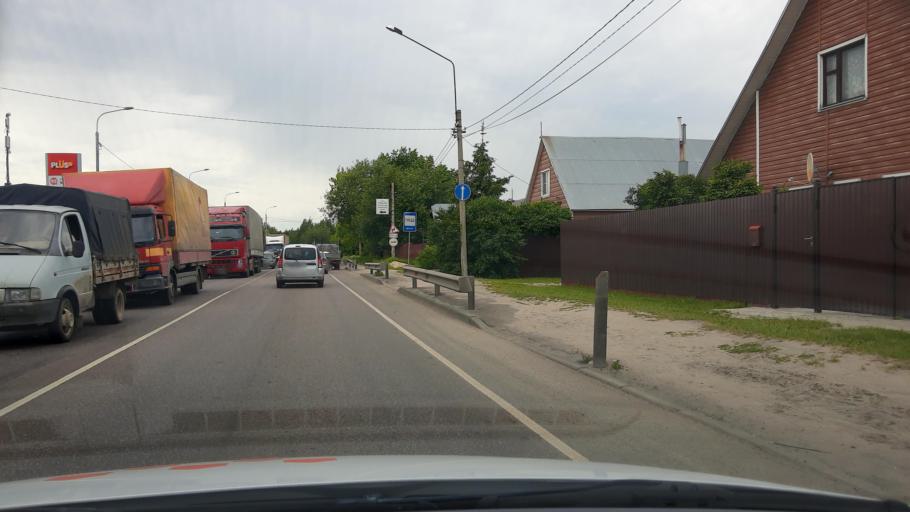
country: RU
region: Moskovskaya
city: Noginsk
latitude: 55.8693
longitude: 38.4370
